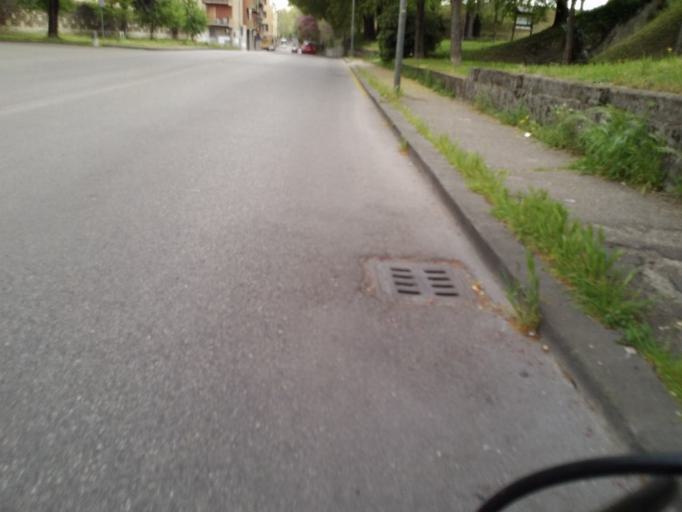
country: IT
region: Veneto
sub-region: Provincia di Verona
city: Verona
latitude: 45.4386
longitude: 10.9782
